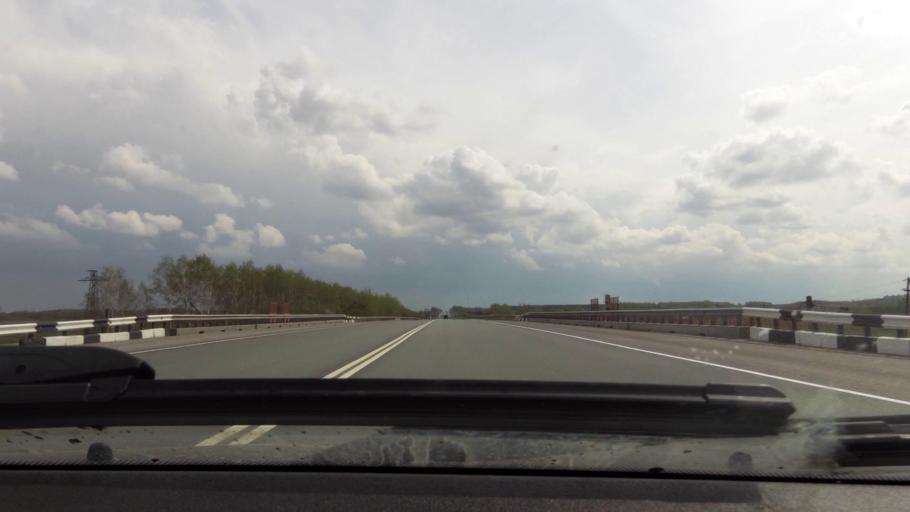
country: RU
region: Rjazan
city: Bagramovo
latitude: 54.7363
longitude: 39.4522
